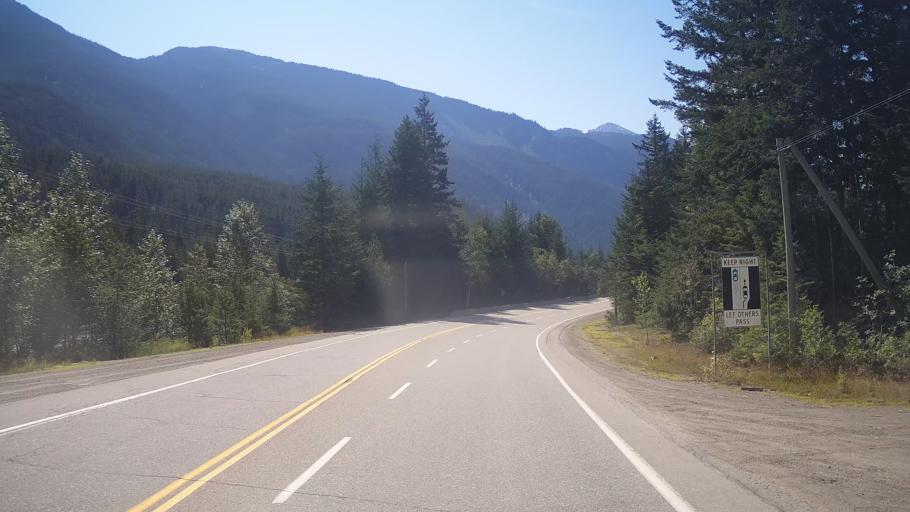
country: CA
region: British Columbia
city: Pemberton
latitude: 50.2556
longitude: -122.8608
